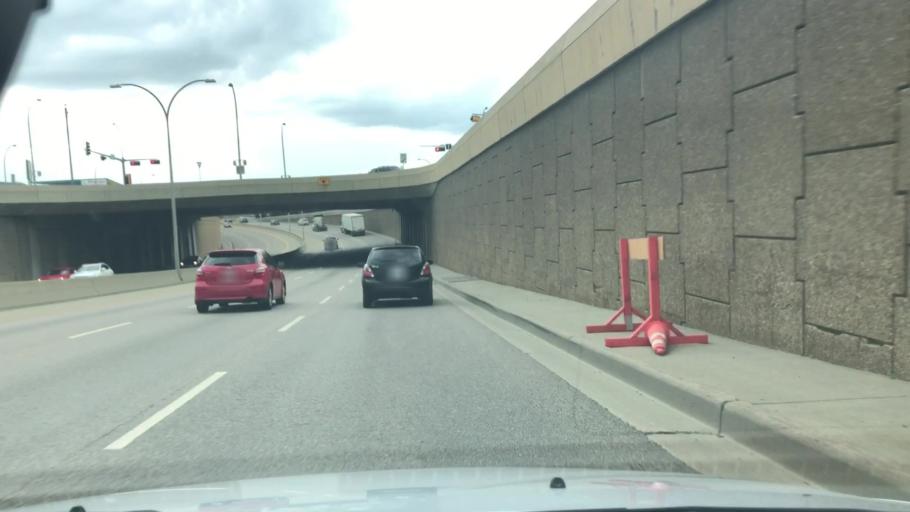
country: CA
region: Alberta
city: Edmonton
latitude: 53.5824
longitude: -113.4659
